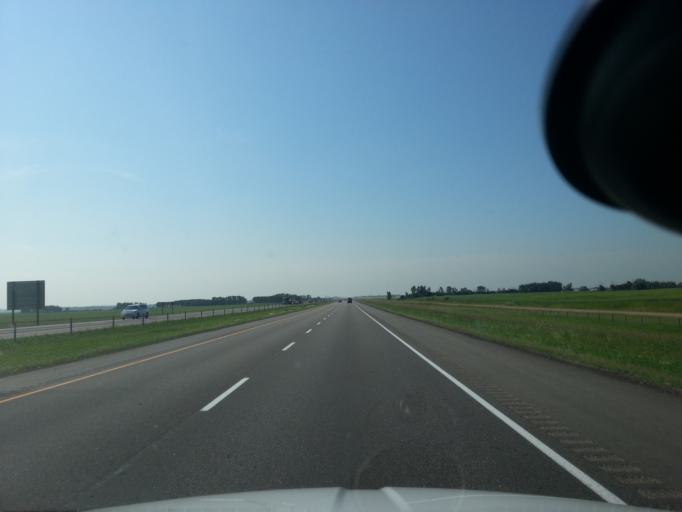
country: CA
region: Alberta
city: Olds
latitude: 51.7793
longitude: -114.0256
